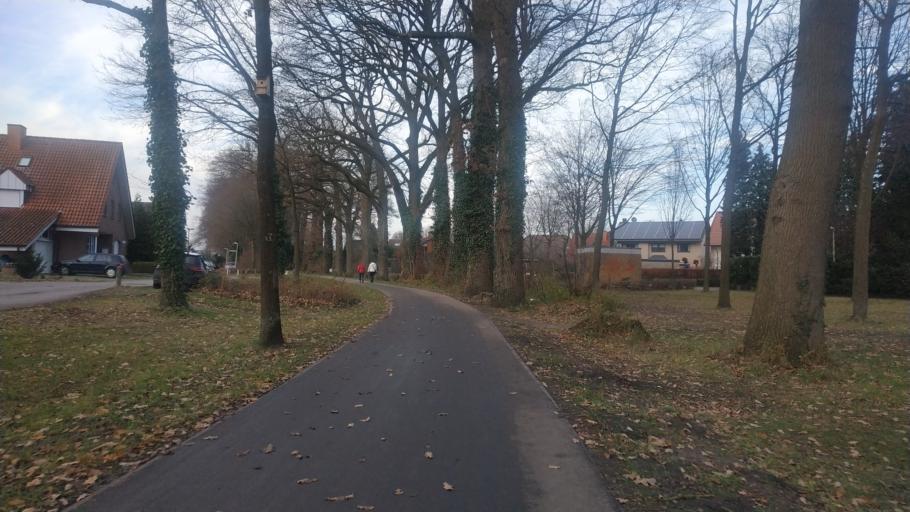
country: DE
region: North Rhine-Westphalia
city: Ibbenburen
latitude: 52.2712
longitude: 7.6999
